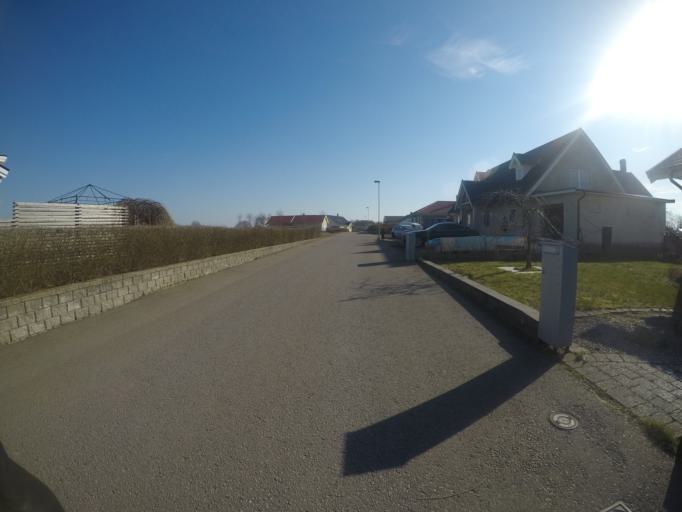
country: SE
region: Halland
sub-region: Laholms Kommun
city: Laholm
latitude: 56.5054
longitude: 13.0662
